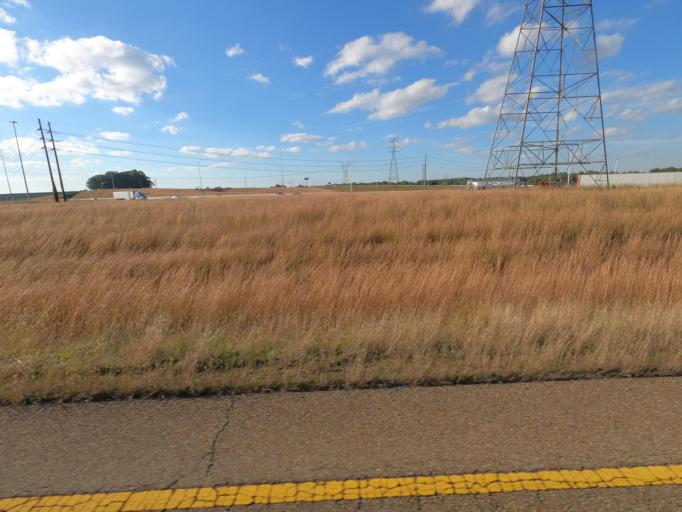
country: US
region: Tennessee
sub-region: Madison County
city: Jackson
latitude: 35.6791
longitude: -88.7761
